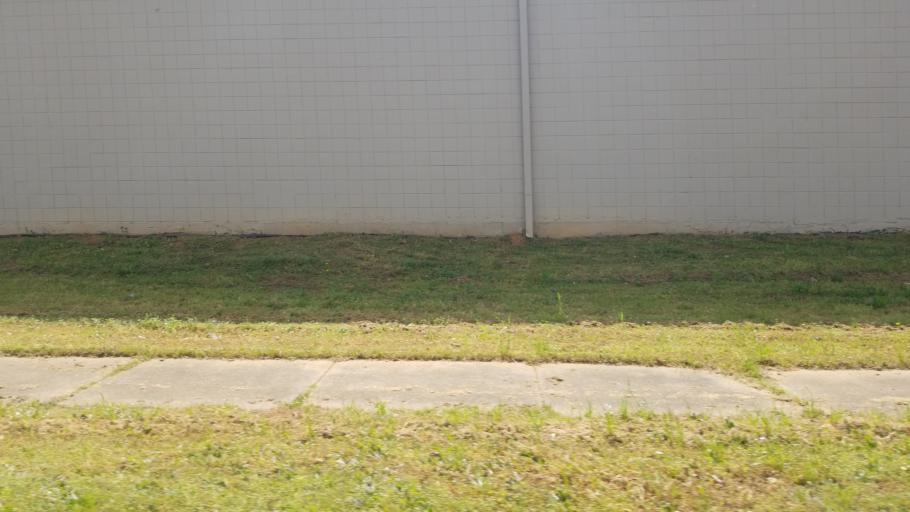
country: US
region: Alabama
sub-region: Montgomery County
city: Montgomery
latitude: 32.3674
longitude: -86.3007
